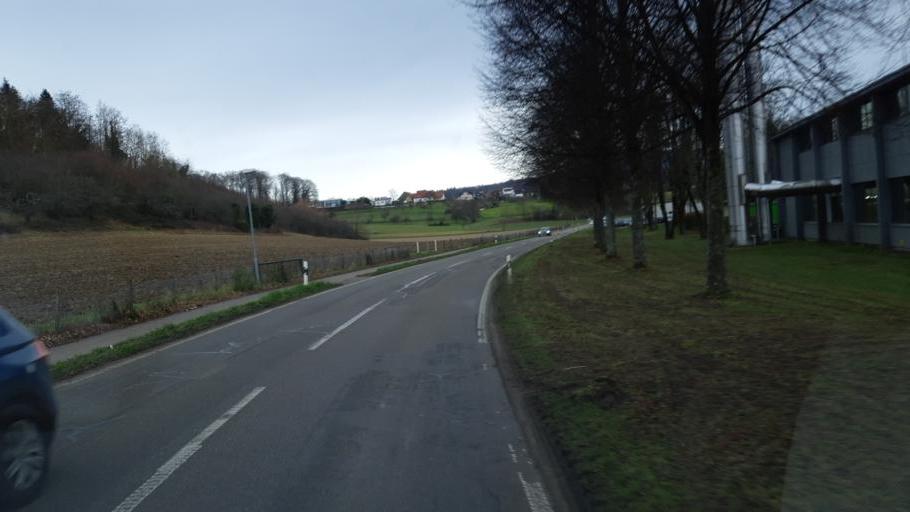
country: DE
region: Baden-Wuerttemberg
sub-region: Freiburg Region
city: Emmendingen
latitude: 48.1183
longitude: 7.8674
